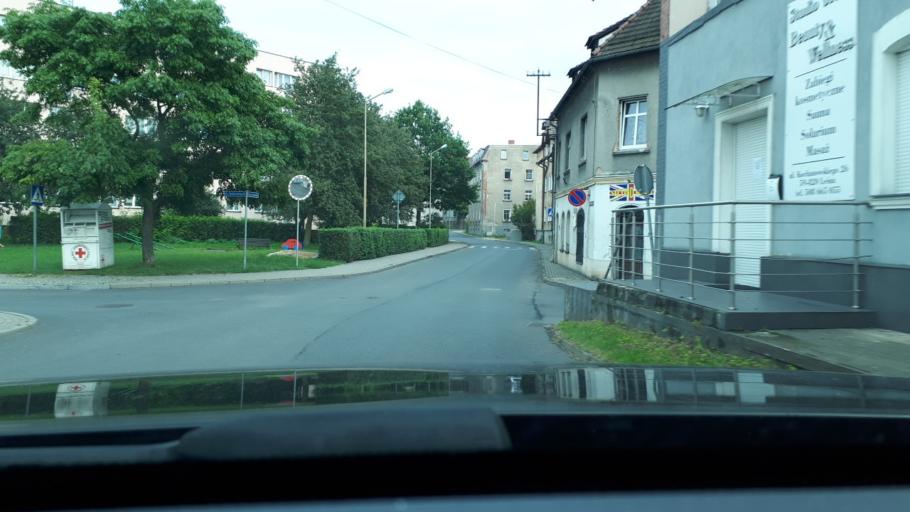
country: PL
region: Lower Silesian Voivodeship
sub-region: Powiat lubanski
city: Lesna
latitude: 51.0219
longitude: 15.2606
